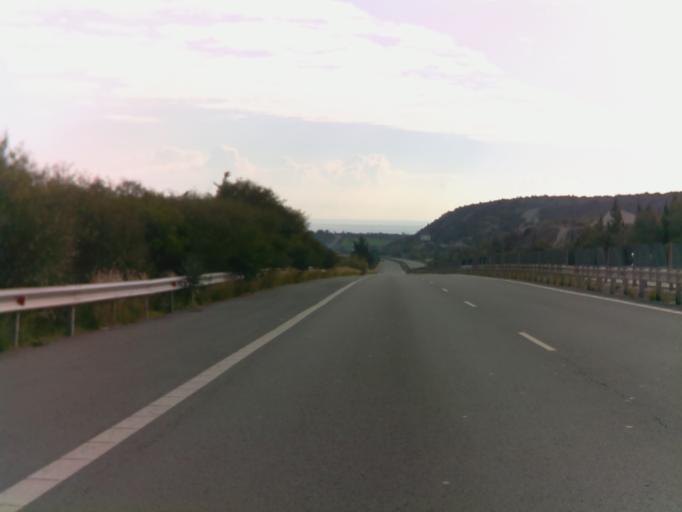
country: CY
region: Limassol
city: Pyrgos
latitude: 34.7236
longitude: 33.2508
